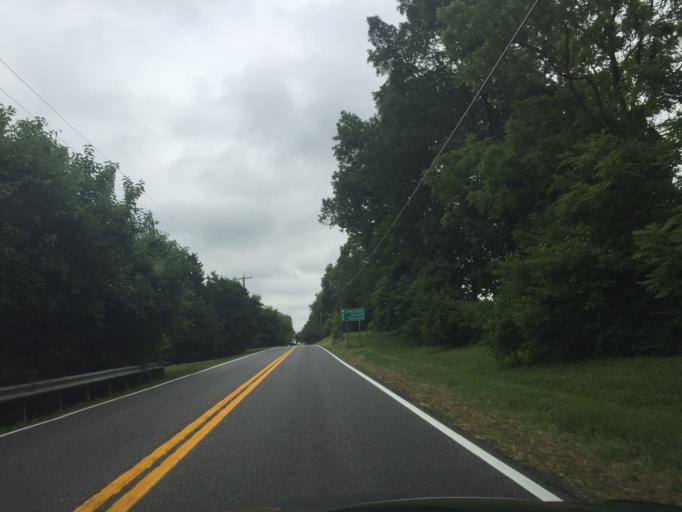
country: US
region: Maryland
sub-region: Harford County
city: Jarrettsville
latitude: 39.5724
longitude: -76.5196
